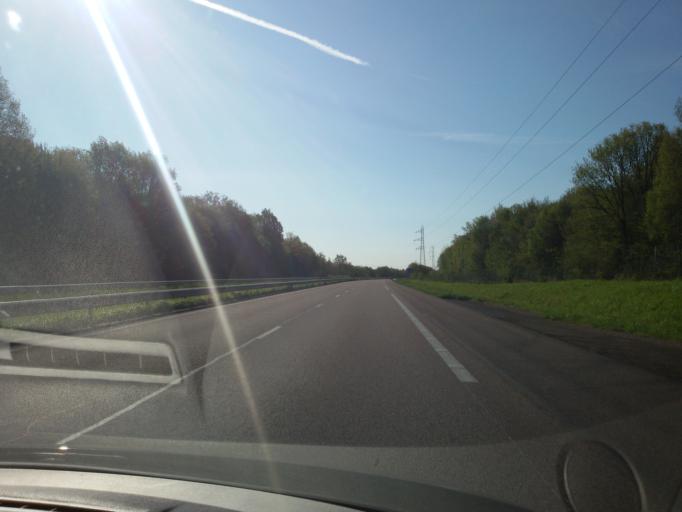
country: FR
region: Centre
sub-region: Departement du Loiret
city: Courtenay
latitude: 48.0723
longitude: 3.0704
